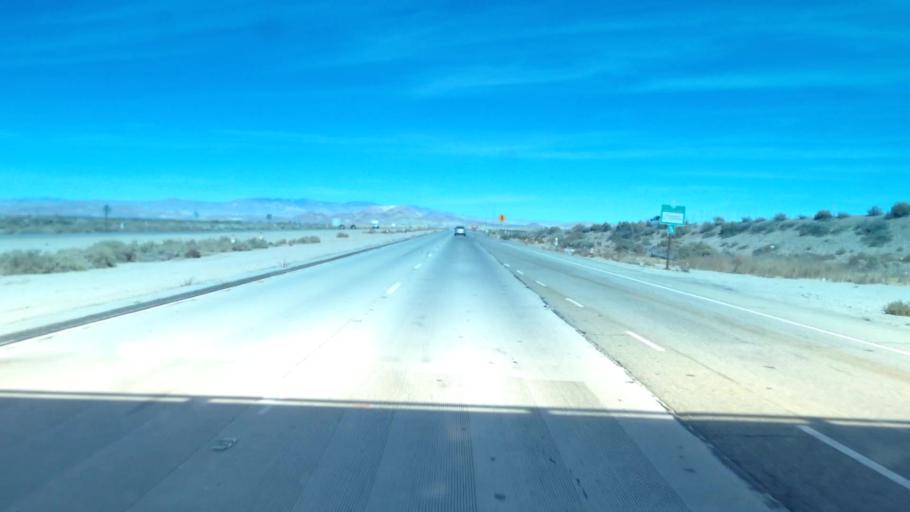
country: US
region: California
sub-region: Los Angeles County
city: Lancaster
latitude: 34.7771
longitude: -118.1705
